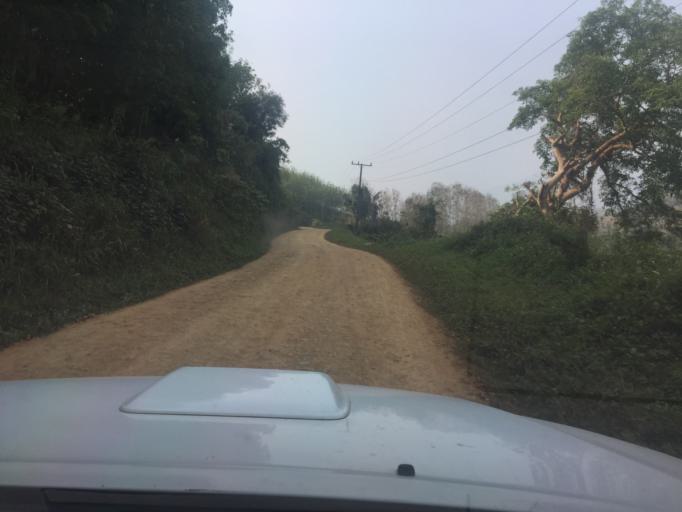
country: TH
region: Phayao
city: Phu Sang
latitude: 19.6648
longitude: 100.5296
